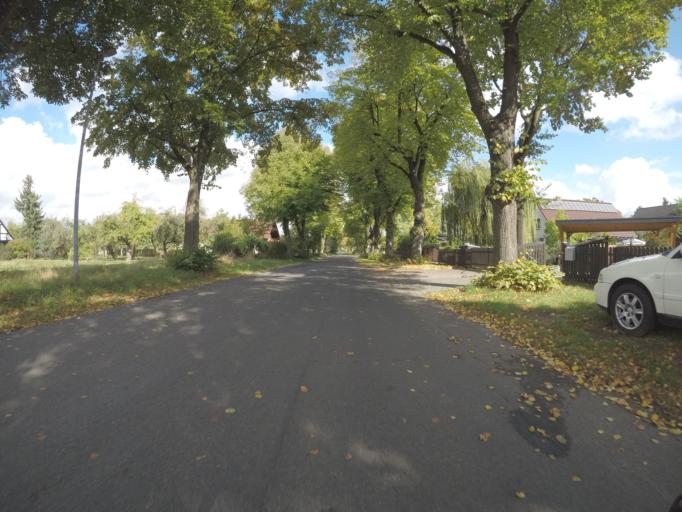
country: DE
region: Brandenburg
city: Ahrensfelde
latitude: 52.5731
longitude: 13.6199
